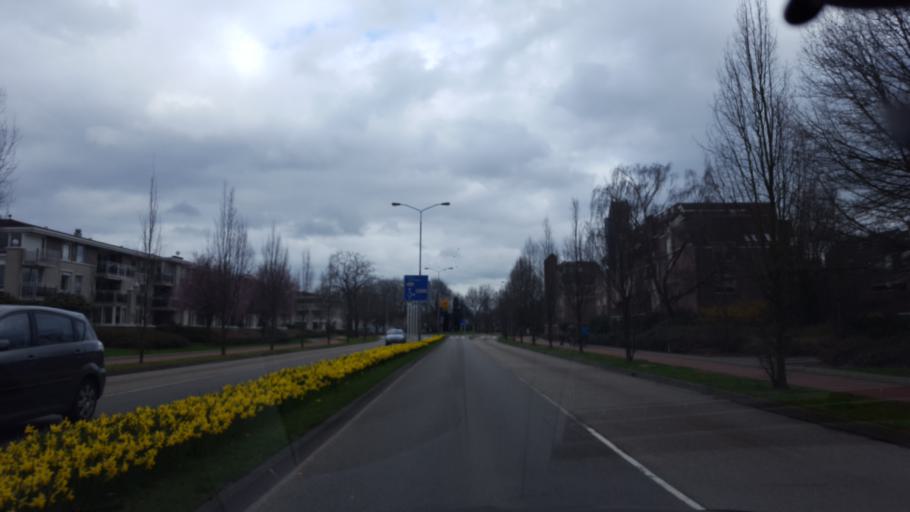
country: NL
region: North Brabant
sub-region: Gemeente Veldhoven
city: Veldhoven
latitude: 51.4208
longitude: 5.4086
